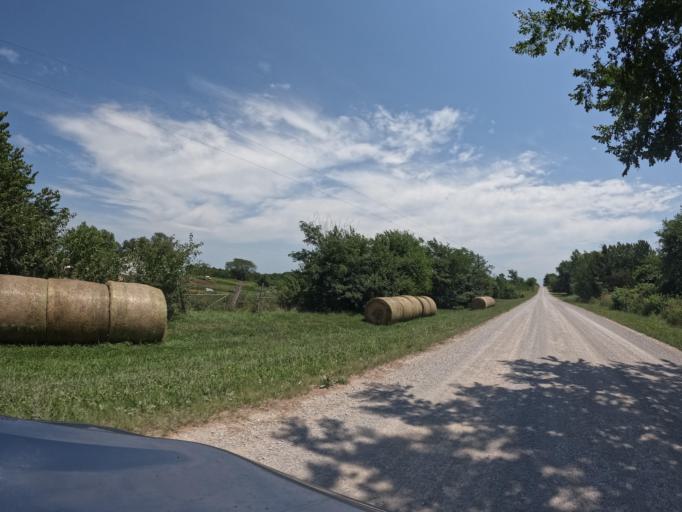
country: US
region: Iowa
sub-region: Appanoose County
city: Centerville
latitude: 40.7867
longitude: -92.9329
